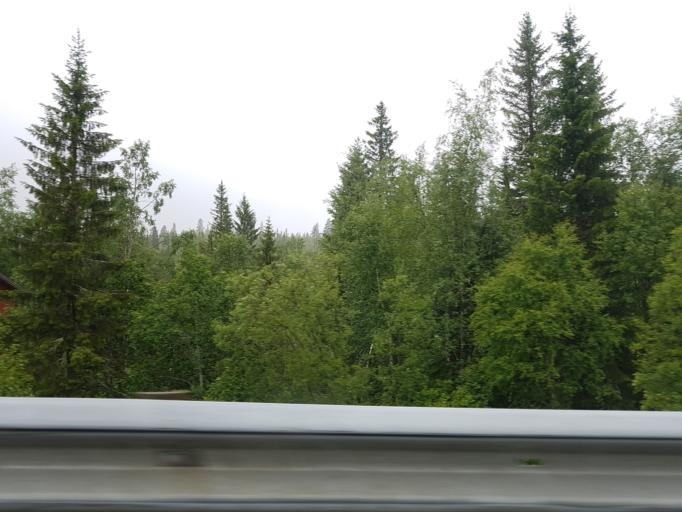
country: NO
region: Sor-Trondelag
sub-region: Selbu
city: Mebonden
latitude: 63.3415
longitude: 11.0780
